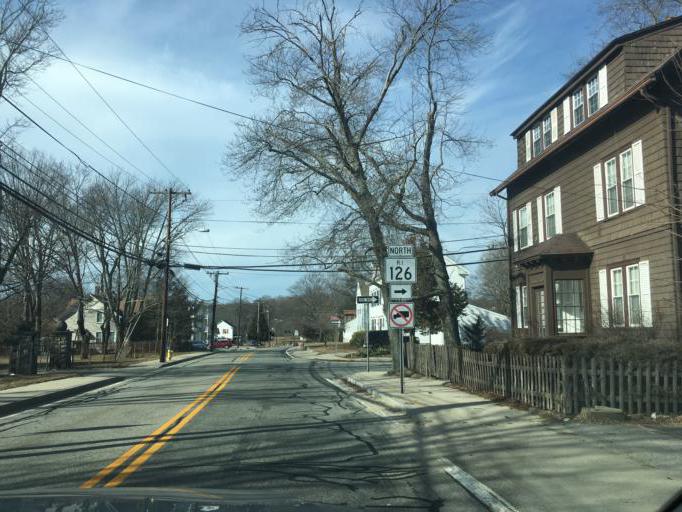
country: US
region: Rhode Island
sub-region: Providence County
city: Central Falls
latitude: 41.9007
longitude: -71.4172
